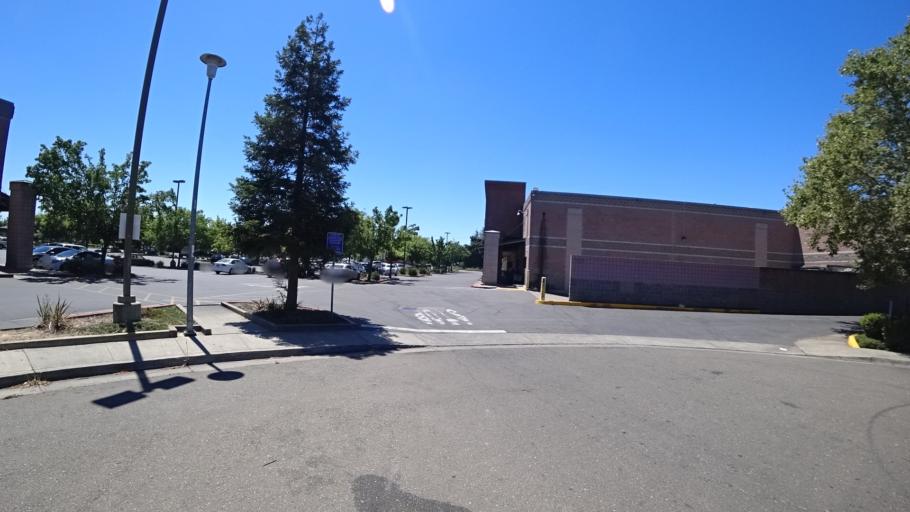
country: US
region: California
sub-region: Sacramento County
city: Sacramento
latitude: 38.5479
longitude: -121.4555
